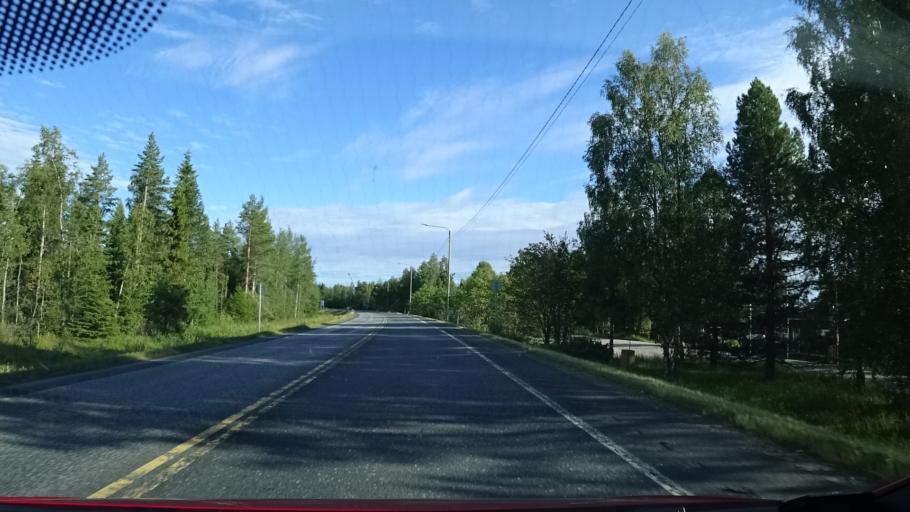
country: FI
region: Northern Ostrobothnia
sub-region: Oulunkaari
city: Kuivaniemi
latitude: 65.5254
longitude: 25.2600
